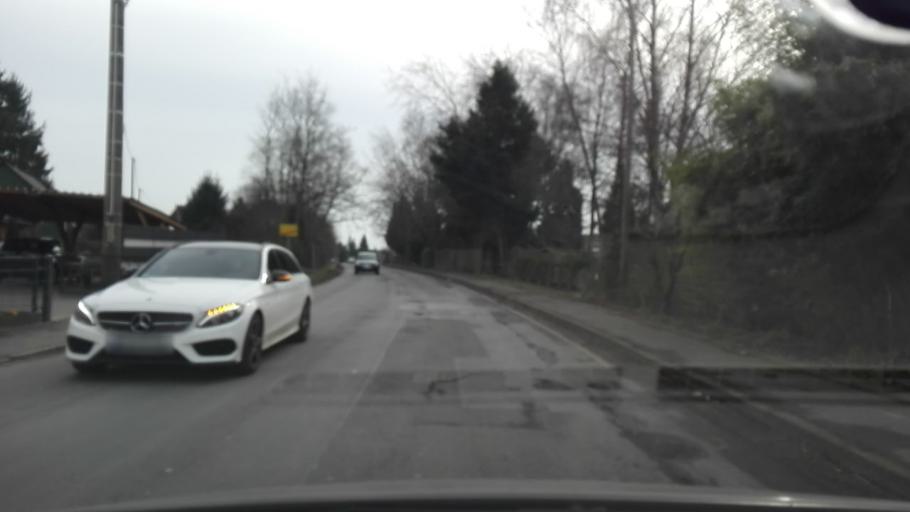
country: DE
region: North Rhine-Westphalia
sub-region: Regierungsbezirk Arnsberg
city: Holzwickede
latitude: 51.4774
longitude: 7.5984
